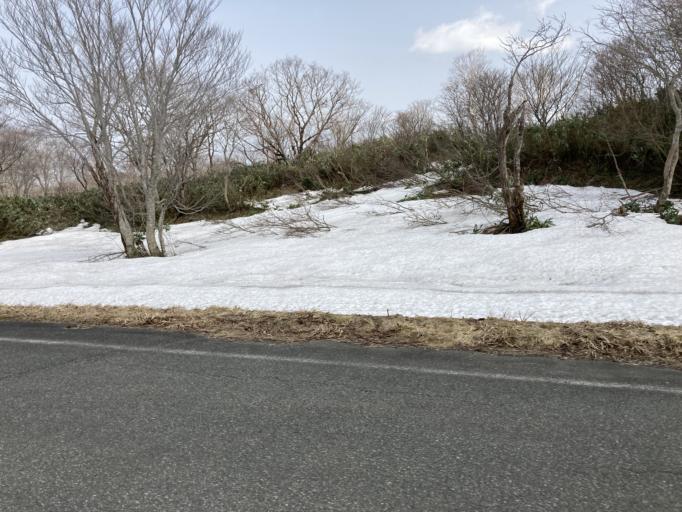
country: JP
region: Akita
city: Yuzawa
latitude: 38.9898
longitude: 140.7635
